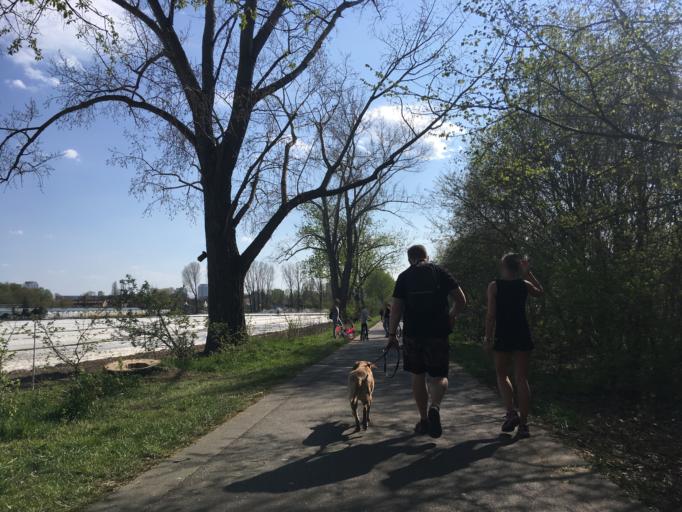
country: DE
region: Berlin
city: Wartenberg
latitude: 52.5822
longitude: 13.5144
